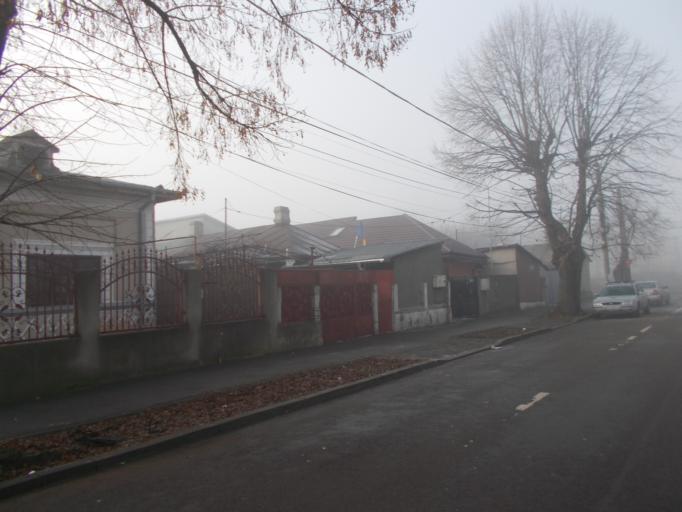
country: RO
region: Ilfov
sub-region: Comuna Jilava
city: Jilava
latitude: 44.3765
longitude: 26.0879
